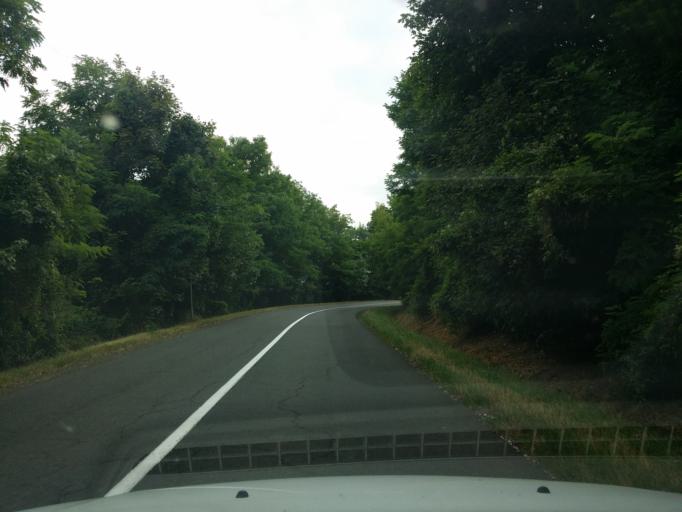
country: HU
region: Nograd
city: Bercel
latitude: 47.9305
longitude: 19.3637
